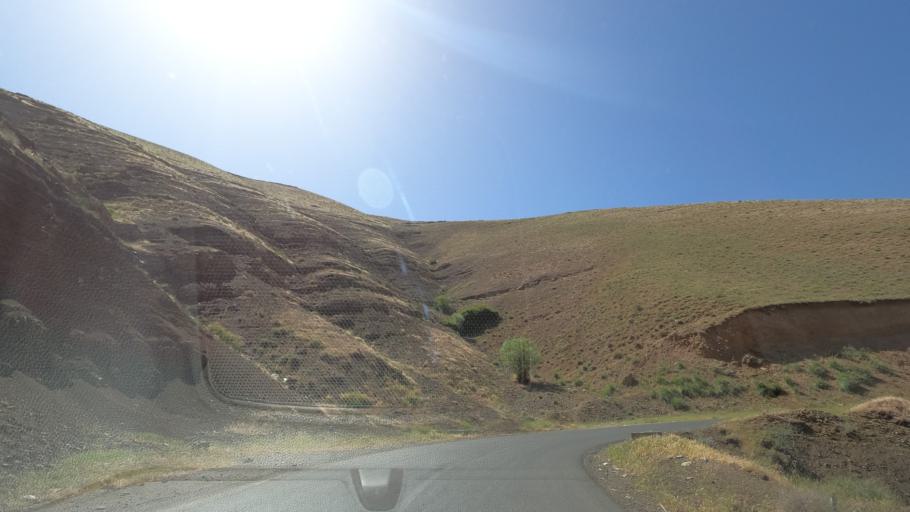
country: IR
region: Alborz
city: Karaj
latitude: 35.9318
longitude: 51.0867
